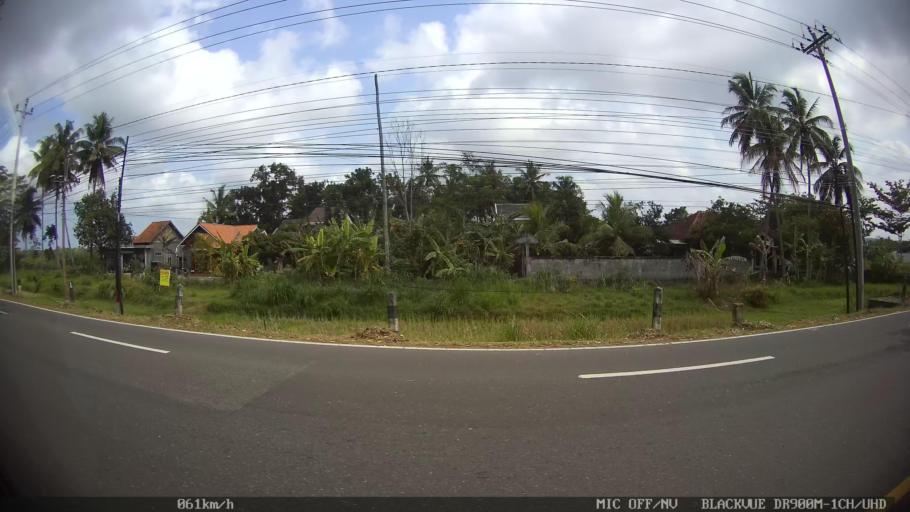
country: ID
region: Daerah Istimewa Yogyakarta
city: Srandakan
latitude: -7.8743
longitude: 110.1365
